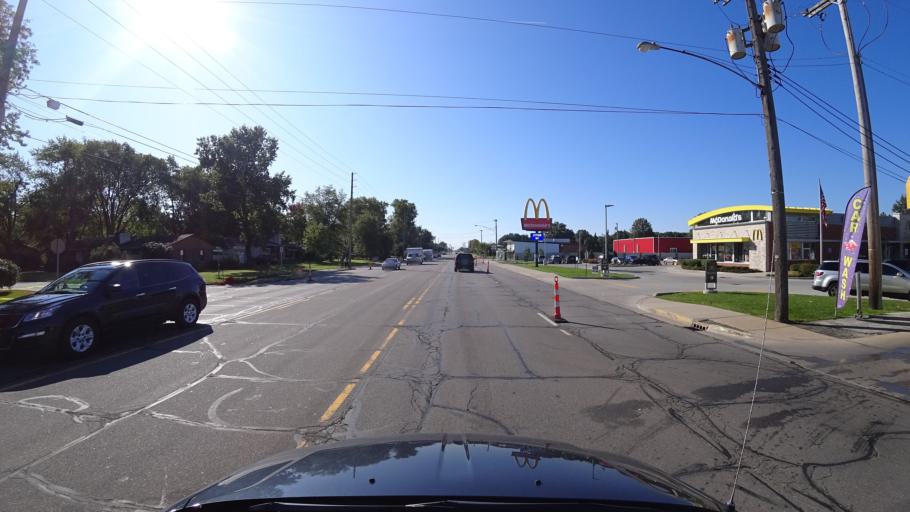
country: US
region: Indiana
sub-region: LaPorte County
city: Michigan City
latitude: 41.6911
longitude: -86.8938
